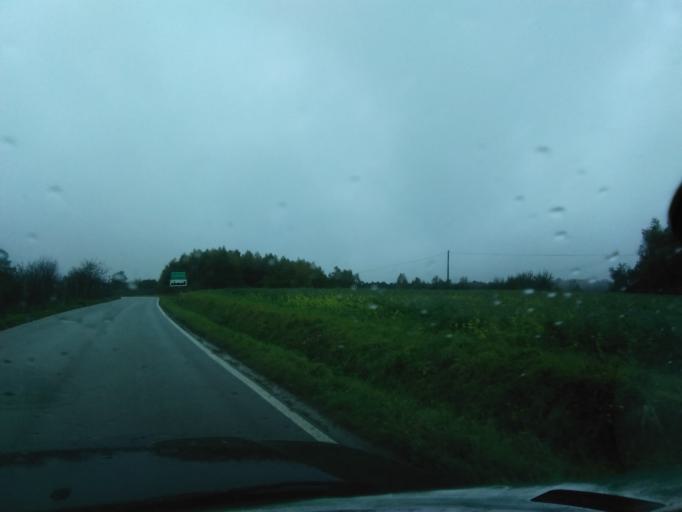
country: PL
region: Subcarpathian Voivodeship
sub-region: Powiat ropczycko-sedziszowski
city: Niedzwiada
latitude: 50.0432
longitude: 21.5420
